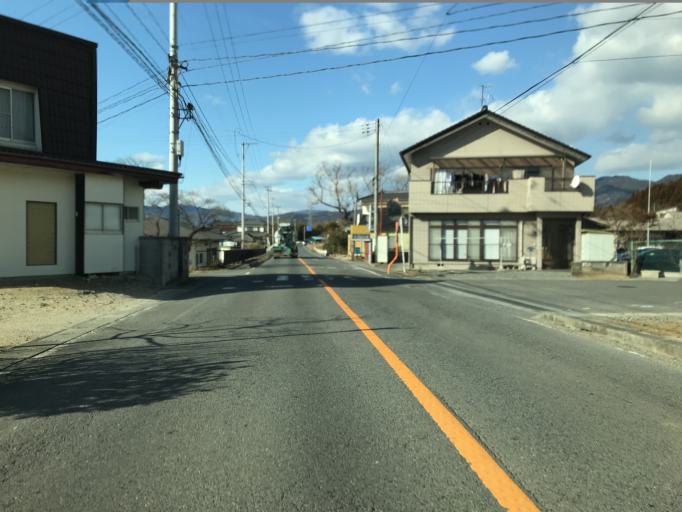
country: JP
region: Fukushima
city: Iwaki
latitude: 37.1129
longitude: 140.8720
